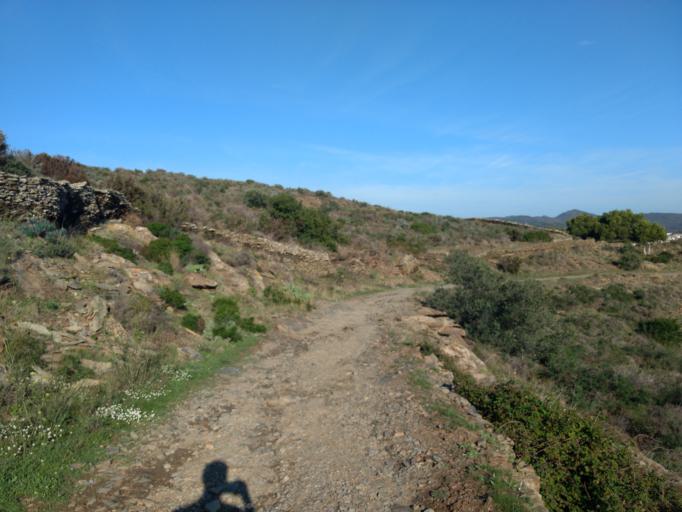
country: ES
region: Catalonia
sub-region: Provincia de Girona
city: Cadaques
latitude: 42.2765
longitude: 3.2783
